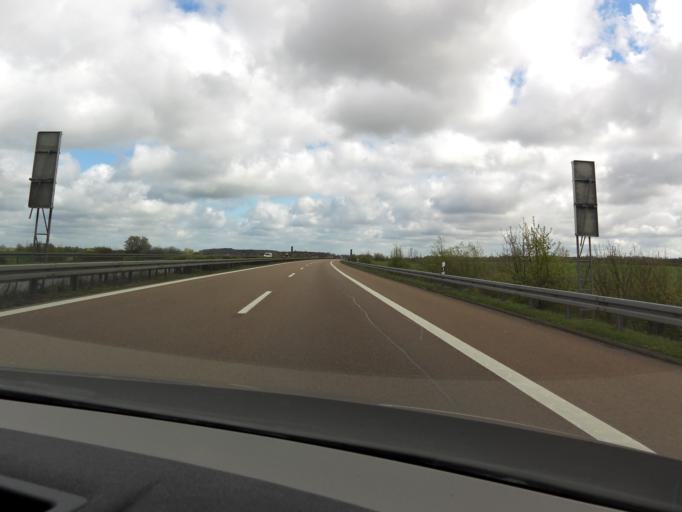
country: DE
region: Mecklenburg-Vorpommern
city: Broderstorf
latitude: 54.0401
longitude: 12.3568
